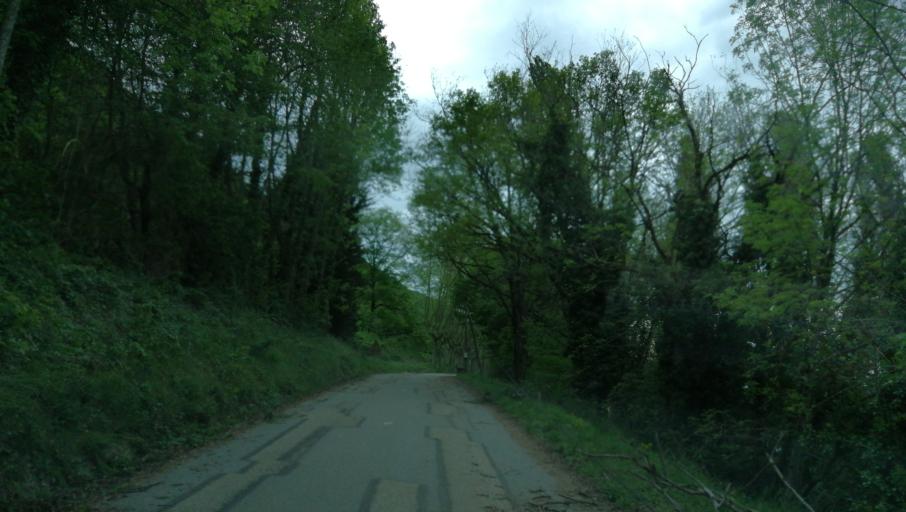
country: FR
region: Rhone-Alpes
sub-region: Departement de la Savoie
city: Chatillon
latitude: 45.7539
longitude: 5.8361
